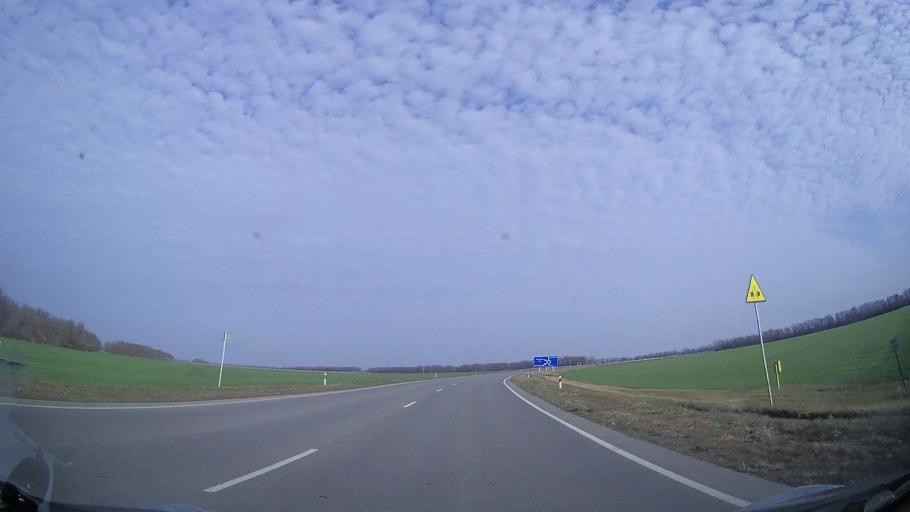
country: RU
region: Rostov
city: Tselina
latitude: 46.5227
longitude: 41.0745
